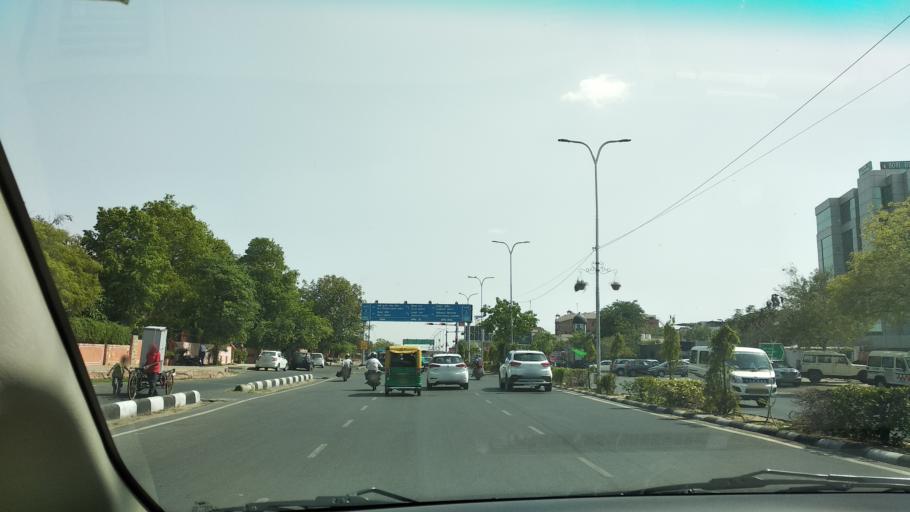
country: IN
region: Rajasthan
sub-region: Jaipur
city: Jaipur
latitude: 26.8962
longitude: 75.8156
